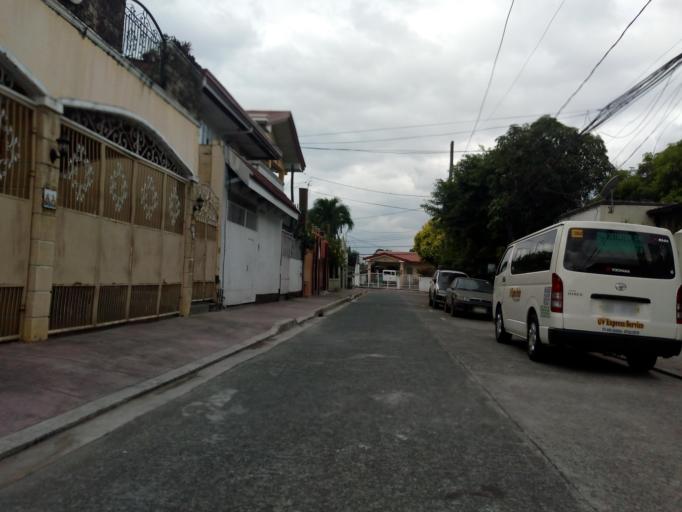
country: PH
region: Calabarzon
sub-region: Province of Rizal
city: Antipolo
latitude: 14.6383
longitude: 121.1174
